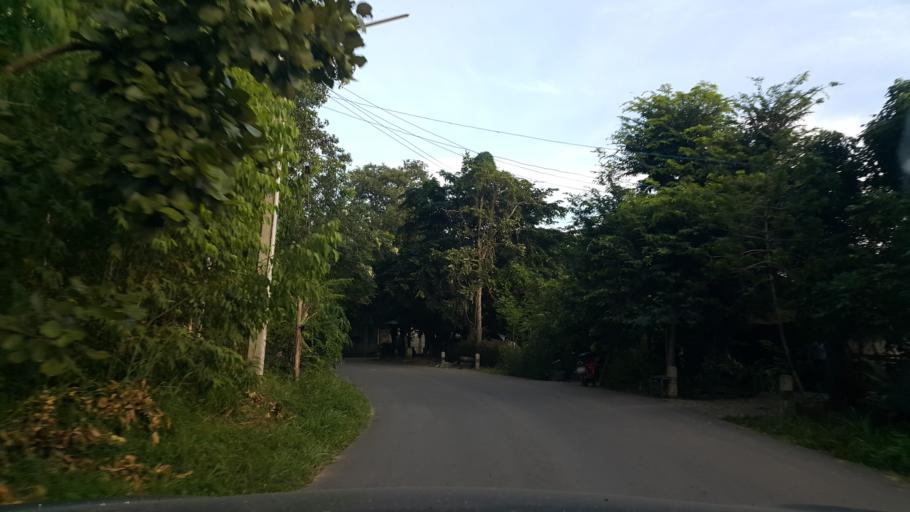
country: TH
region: Chiang Mai
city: San Sai
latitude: 18.9075
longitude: 99.0409
